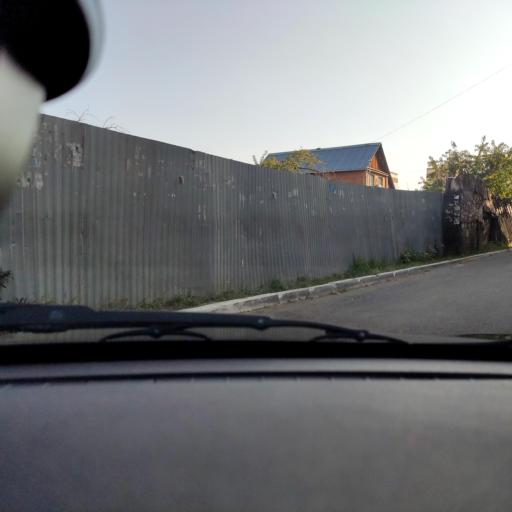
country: RU
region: Samara
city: Tol'yatti
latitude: 53.5248
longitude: 49.4147
